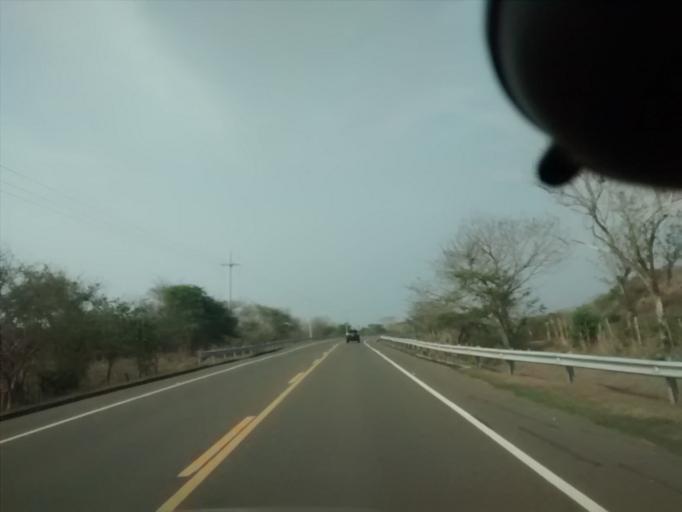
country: CO
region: Bolivar
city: Clemencia
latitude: 10.6341
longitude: -75.4207
